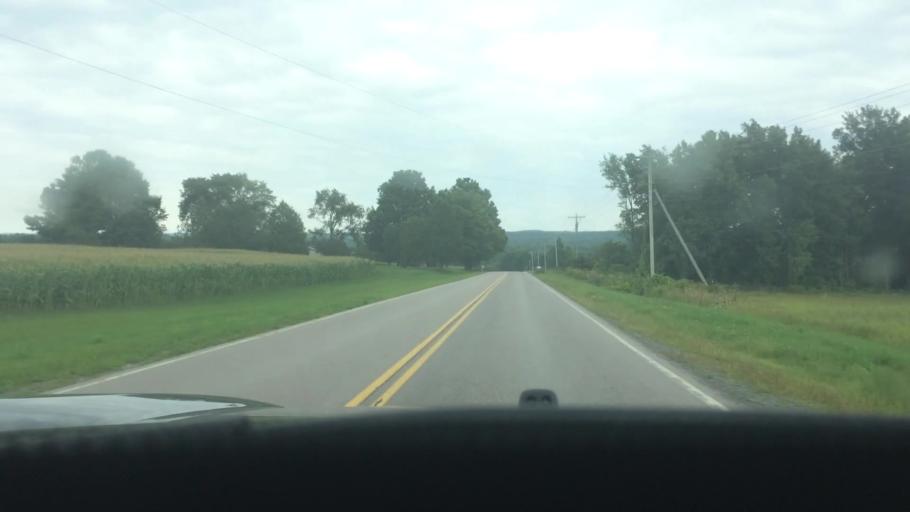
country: US
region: New York
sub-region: St. Lawrence County
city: Canton
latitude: 44.5410
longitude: -75.0835
